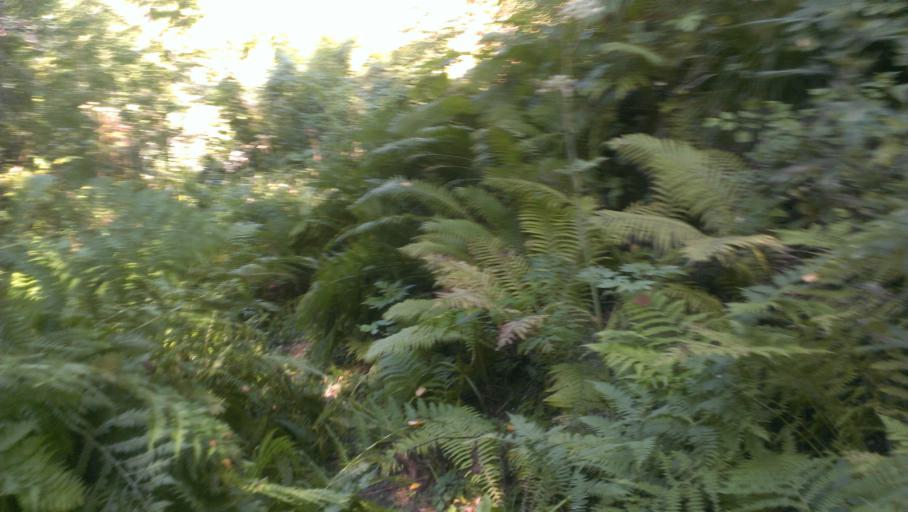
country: RU
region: Altai Krai
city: Nauchnyy Gorodok
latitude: 53.4248
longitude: 83.5049
